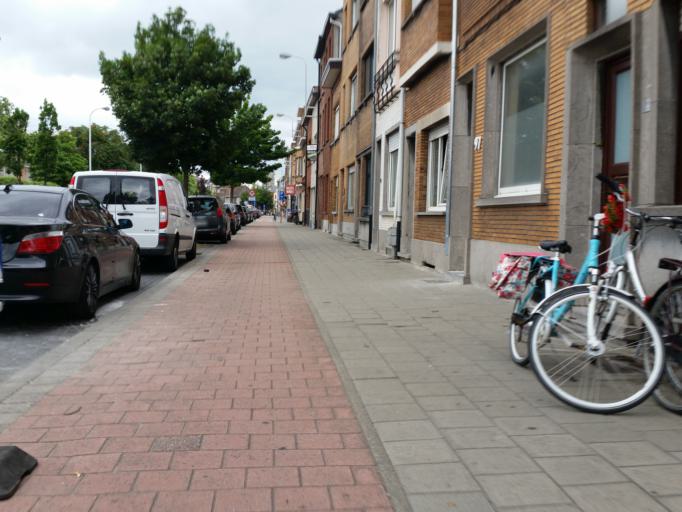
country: BE
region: Flanders
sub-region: Provincie Antwerpen
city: Mechelen
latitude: 51.0190
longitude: 4.4933
